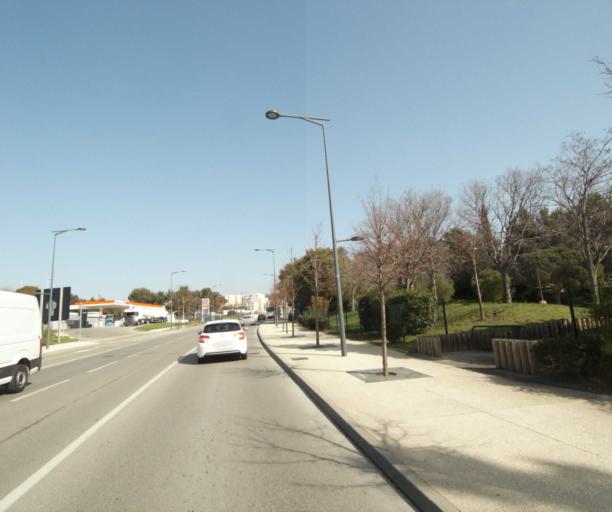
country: FR
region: Provence-Alpes-Cote d'Azur
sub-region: Departement des Bouches-du-Rhone
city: Vitrolles
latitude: 43.4448
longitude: 5.2464
